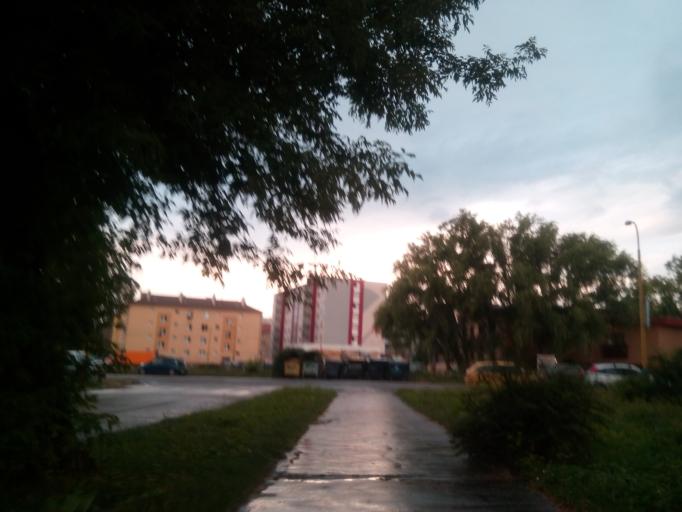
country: SK
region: Kosicky
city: Kosice
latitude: 48.7315
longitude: 21.2559
